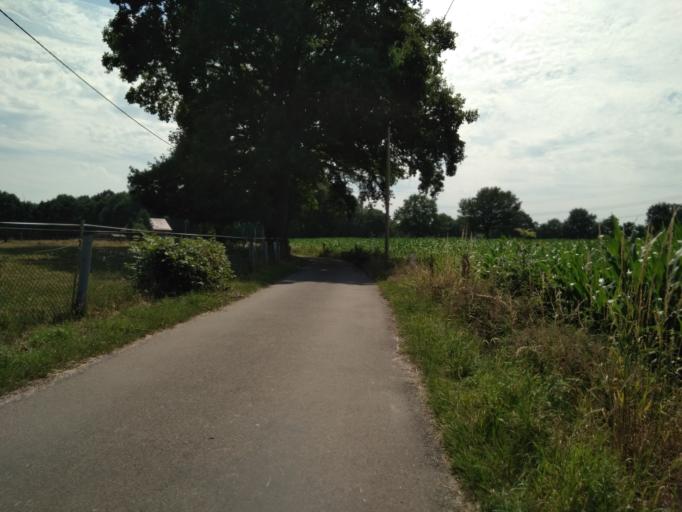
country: DE
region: North Rhine-Westphalia
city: Dorsten
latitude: 51.6502
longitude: 6.9395
